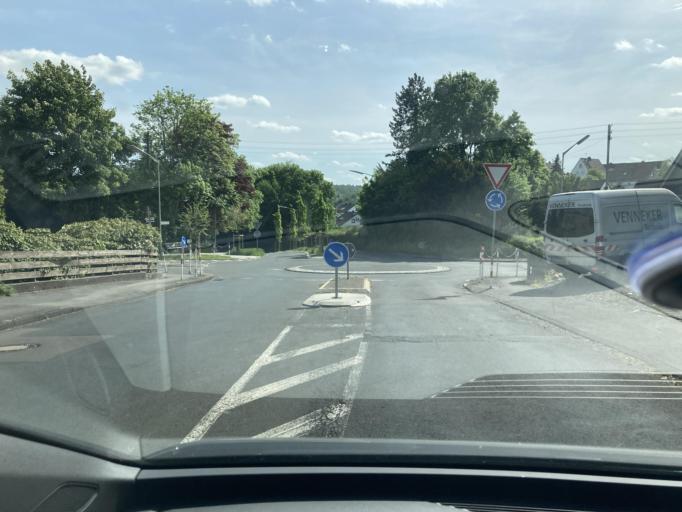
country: DE
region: North Rhine-Westphalia
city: Kreuztal
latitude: 50.9688
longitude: 7.9903
